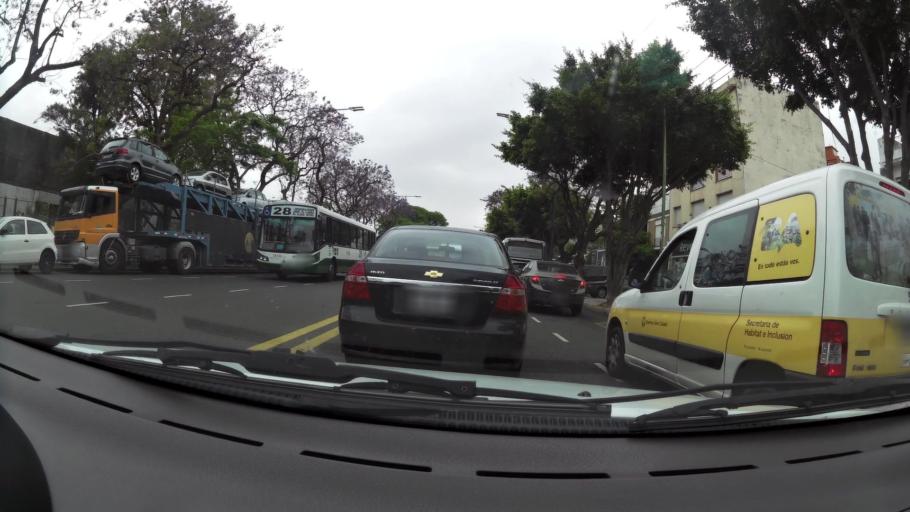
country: AR
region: Buenos Aires F.D.
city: Colegiales
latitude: -34.5477
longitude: -58.4532
